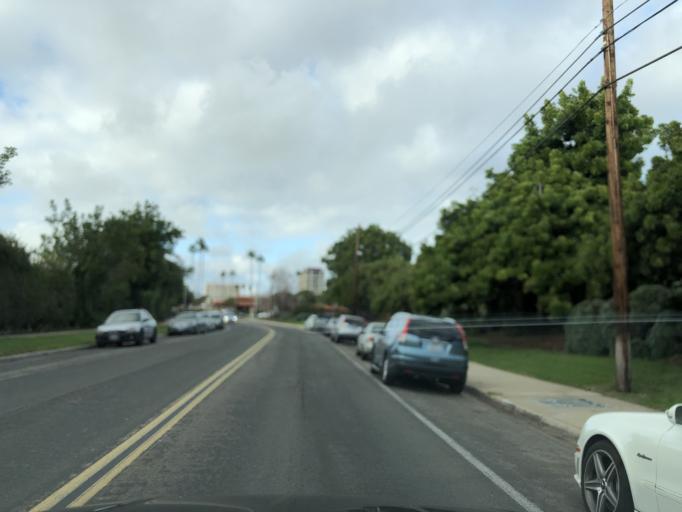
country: US
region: California
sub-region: San Diego County
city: La Jolla
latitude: 32.8151
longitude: -117.1822
